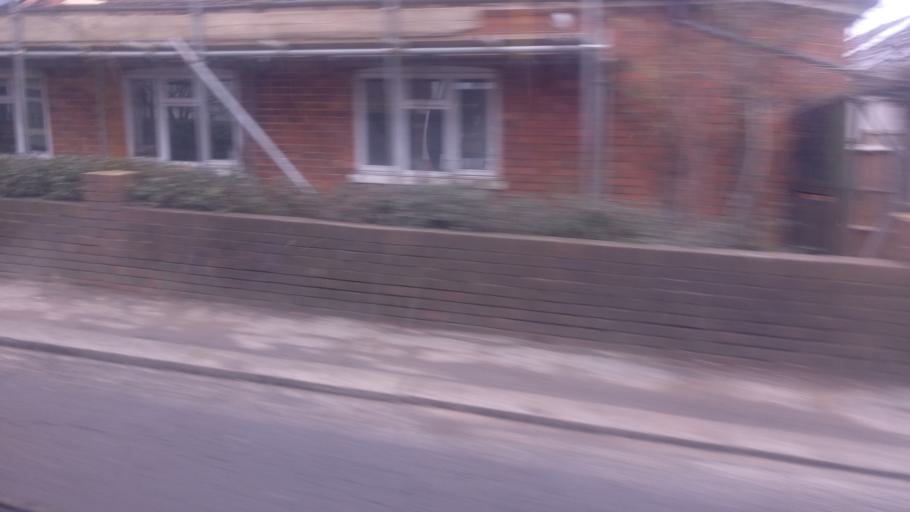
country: GB
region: England
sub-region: Surrey
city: Chertsey
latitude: 51.3862
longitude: -0.5033
